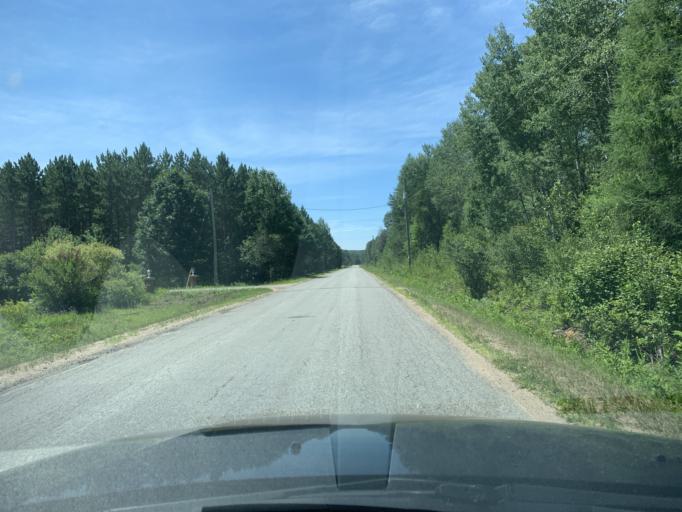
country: CA
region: Ontario
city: Petawawa
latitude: 45.6601
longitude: -77.5948
